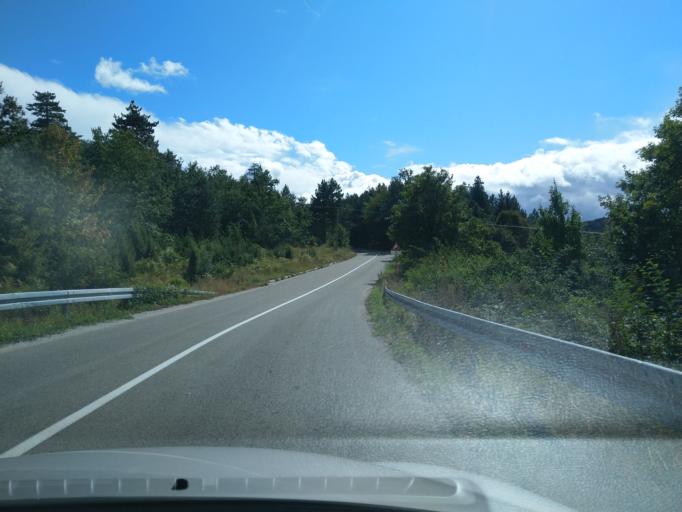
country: RS
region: Central Serbia
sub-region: Zlatiborski Okrug
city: Cajetina
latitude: 43.7252
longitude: 19.8088
